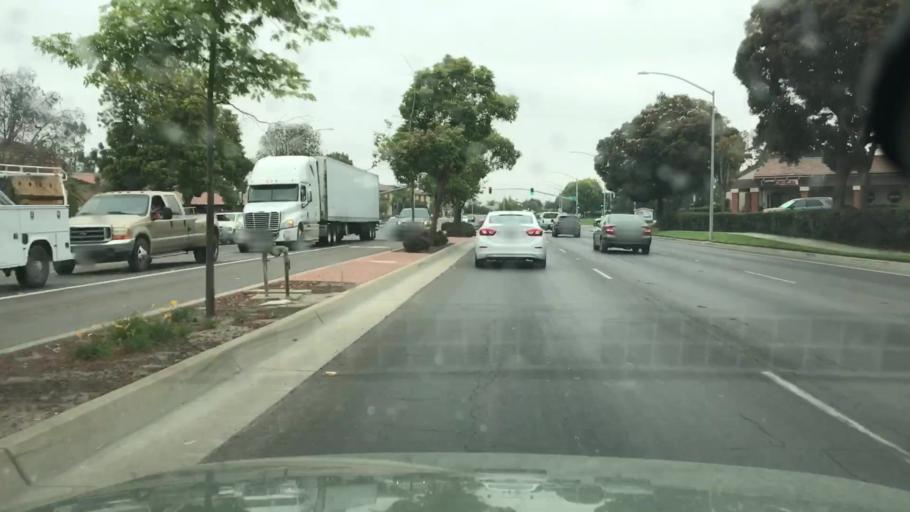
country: US
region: California
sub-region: Santa Barbara County
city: Santa Maria
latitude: 34.9218
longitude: -120.4327
